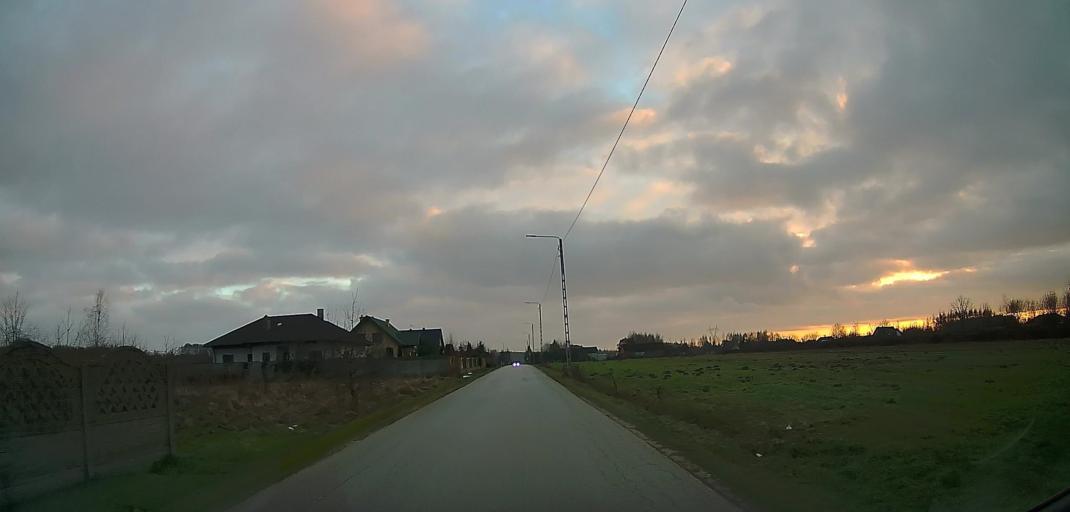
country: PL
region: Masovian Voivodeship
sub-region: Powiat radomski
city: Jedlinsk
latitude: 51.4601
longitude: 21.1234
